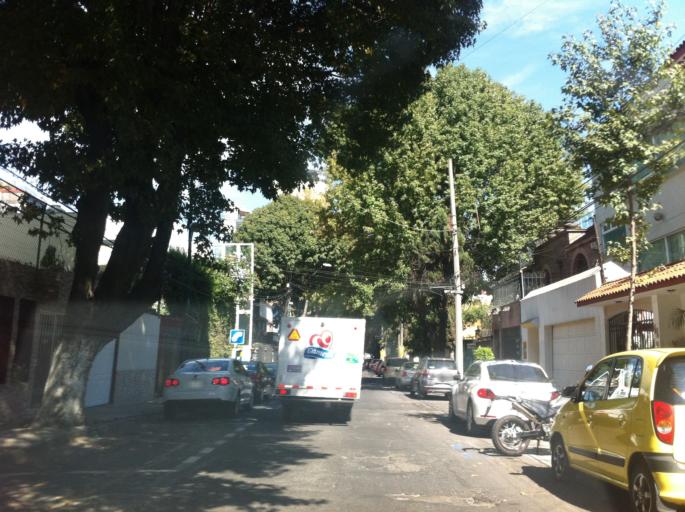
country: MX
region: Mexico City
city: Miguel Hidalgo
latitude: 19.4333
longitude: -99.1783
